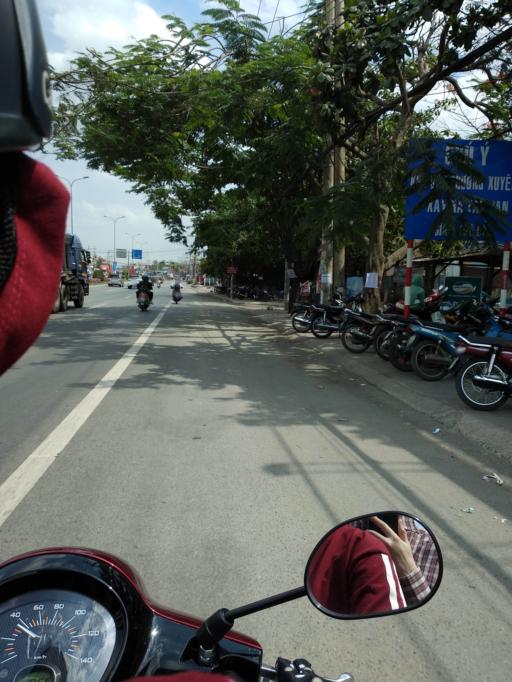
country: VN
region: Ba Ria-Vung Tau
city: Thi Tran Phu My
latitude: 10.6216
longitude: 107.0557
